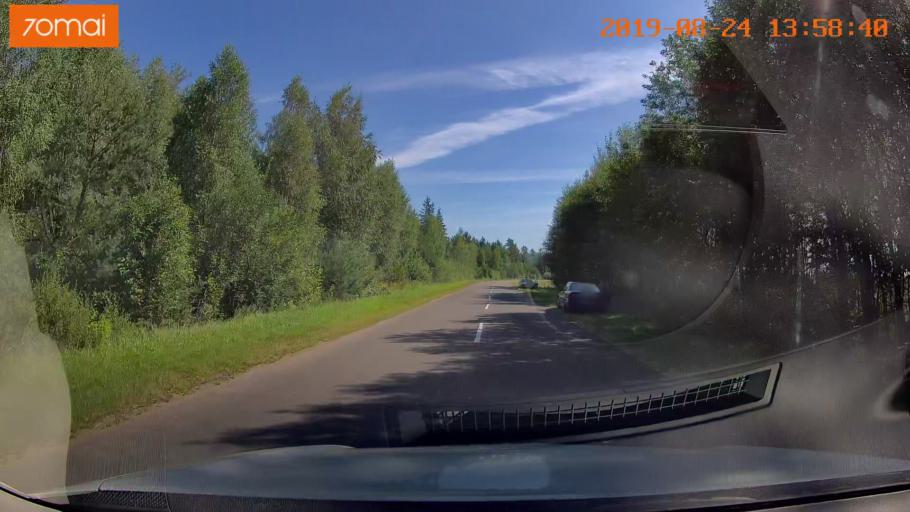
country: BY
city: Michanovichi
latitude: 53.6072
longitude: 27.6758
